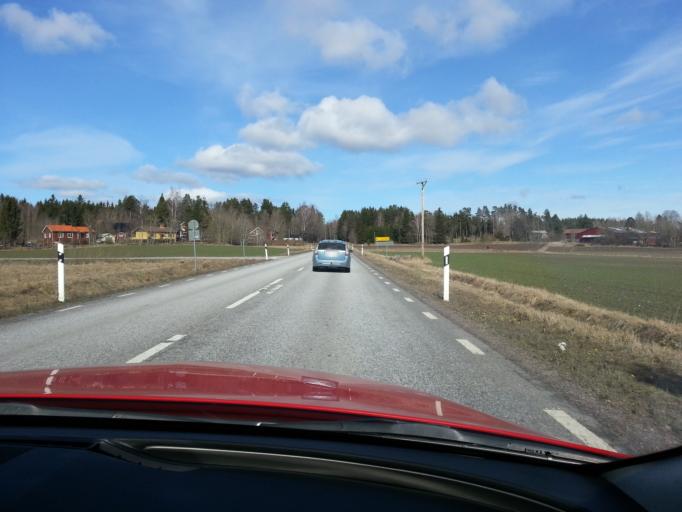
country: SE
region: Uppsala
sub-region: Osthammars Kommun
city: Gimo
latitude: 60.0935
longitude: 18.1227
